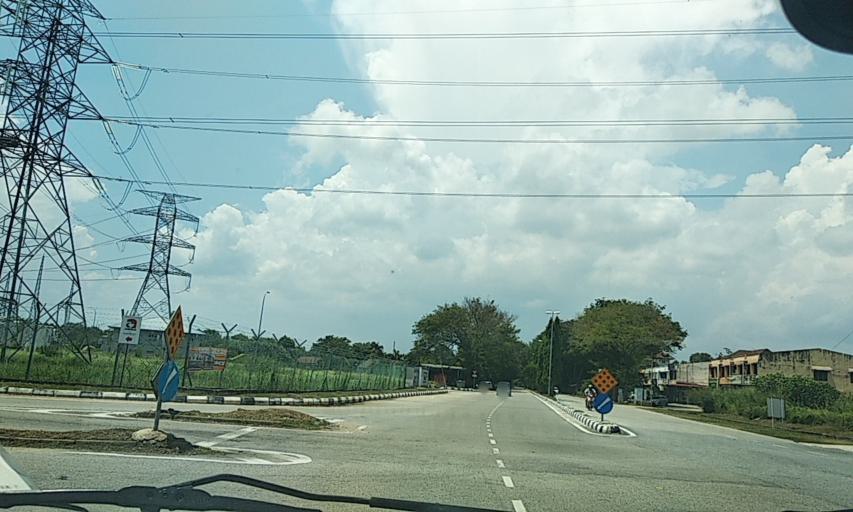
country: MY
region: Kedah
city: Sungai Petani
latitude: 5.6359
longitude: 100.4753
